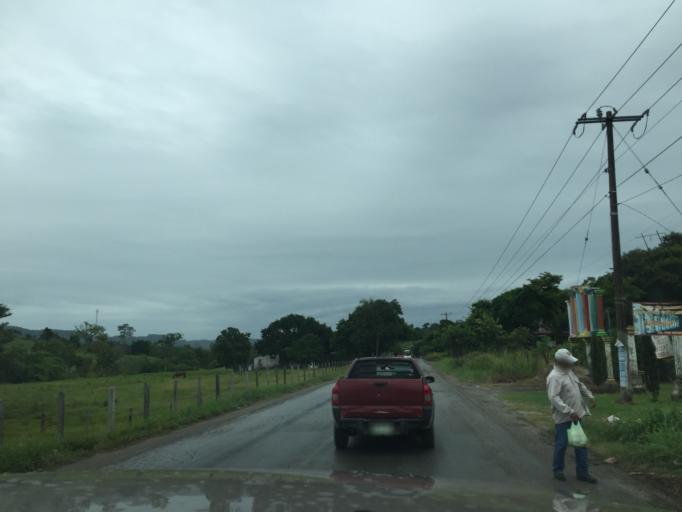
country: MX
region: Veracruz
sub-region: Papantla
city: El Chote
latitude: 20.4415
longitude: -97.4041
